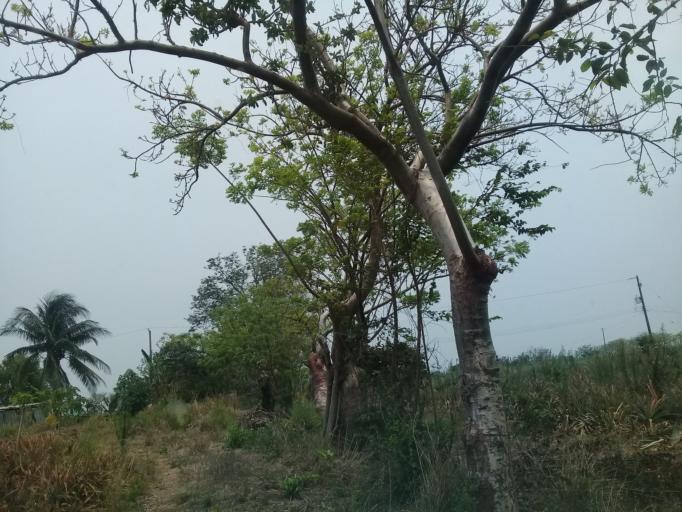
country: MX
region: Veracruz
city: Paso del Toro
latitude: 18.9742
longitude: -96.1392
